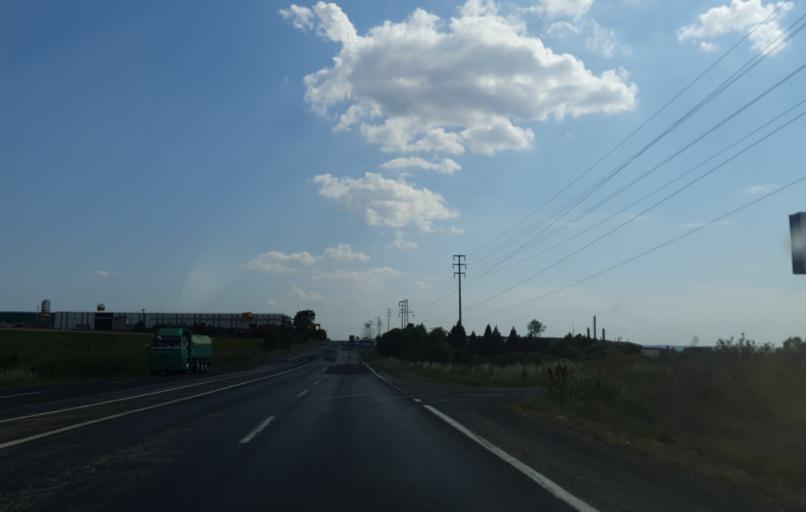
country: TR
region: Kirklareli
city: Buyukkaristiran
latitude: 41.2544
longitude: 27.5440
